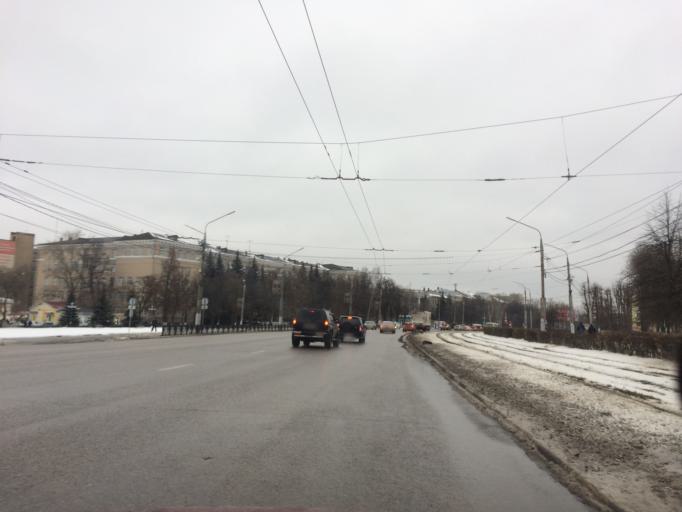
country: RU
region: Tula
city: Mendeleyevskiy
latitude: 54.1647
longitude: 37.5873
